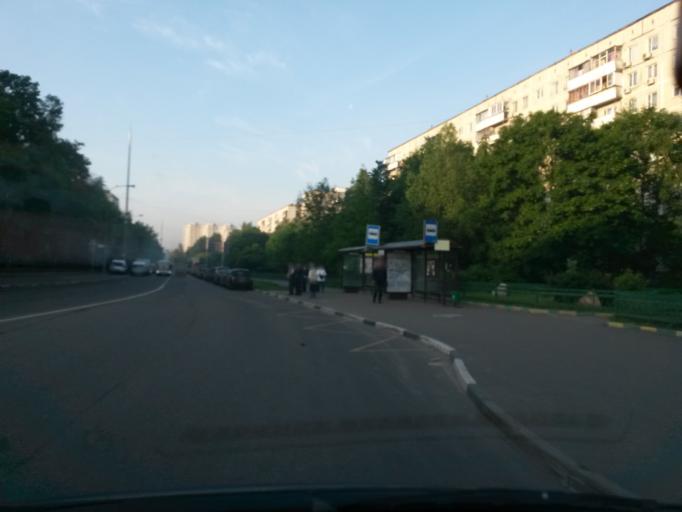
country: RU
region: Moscow
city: Gol'yanovo
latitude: 55.8275
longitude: 37.8247
